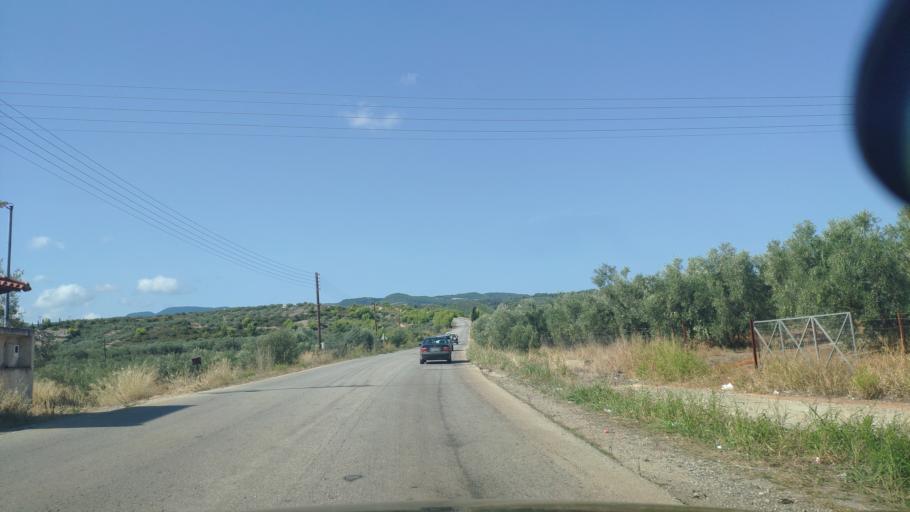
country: GR
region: Peloponnese
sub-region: Nomos Korinthias
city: Moulki
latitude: 37.9904
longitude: 22.6967
